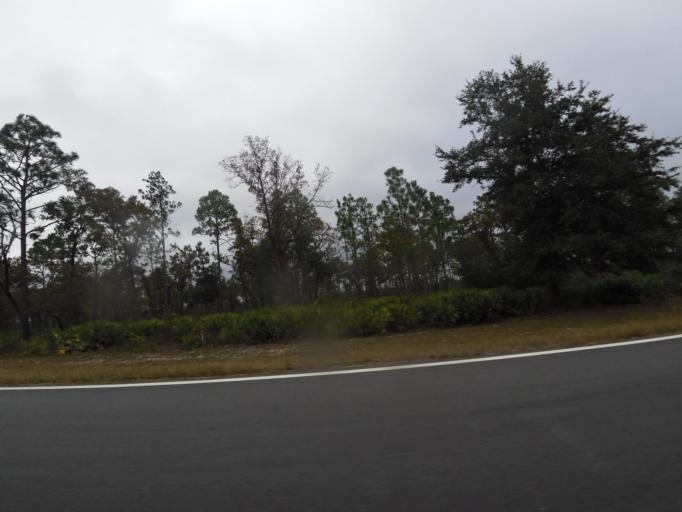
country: US
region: Georgia
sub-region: Charlton County
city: Folkston
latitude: 30.7417
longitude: -82.1276
